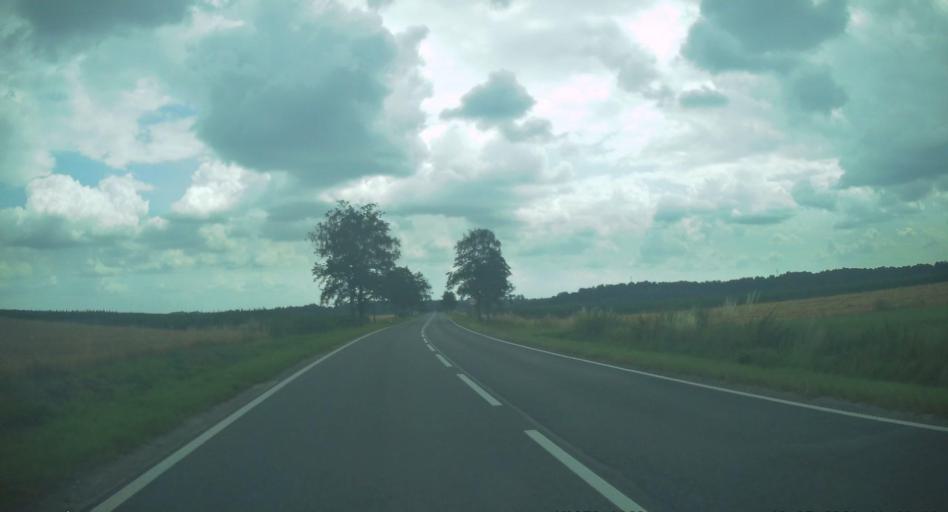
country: PL
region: Opole Voivodeship
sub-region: Powiat prudnicki
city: Laka Prudnicka
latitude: 50.4115
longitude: 17.5010
